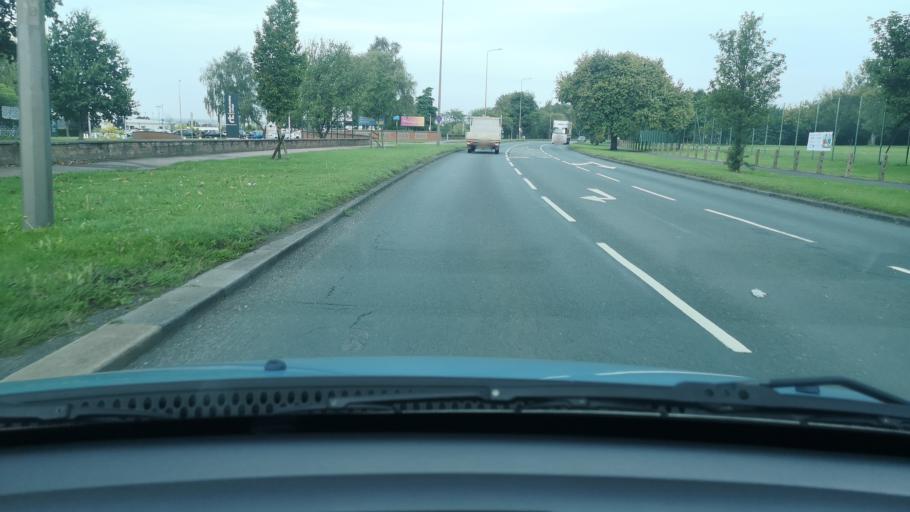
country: GB
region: England
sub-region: North Lincolnshire
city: Scunthorpe
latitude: 53.5791
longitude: -0.6647
